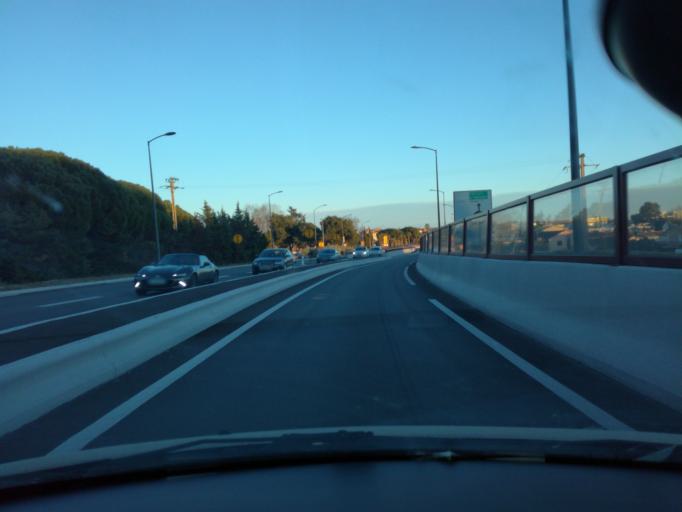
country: FR
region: Provence-Alpes-Cote d'Azur
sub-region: Departement du Var
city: Puget-sur-Argens
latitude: 43.4568
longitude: 6.6876
